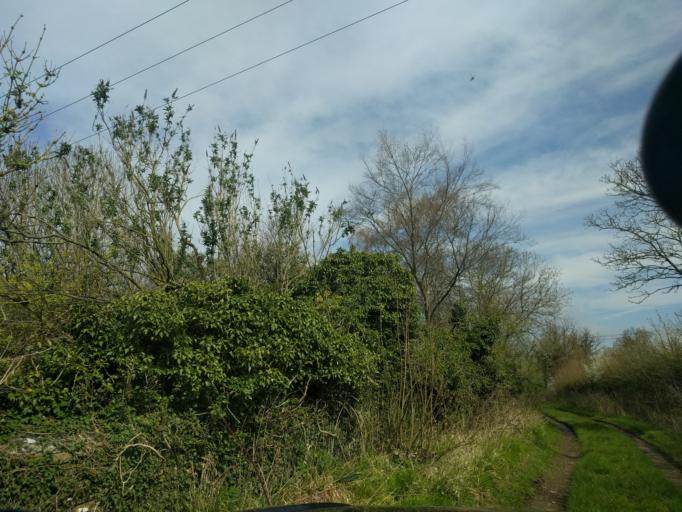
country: GB
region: England
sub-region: Wiltshire
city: Corsham
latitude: 51.4437
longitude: -2.1567
